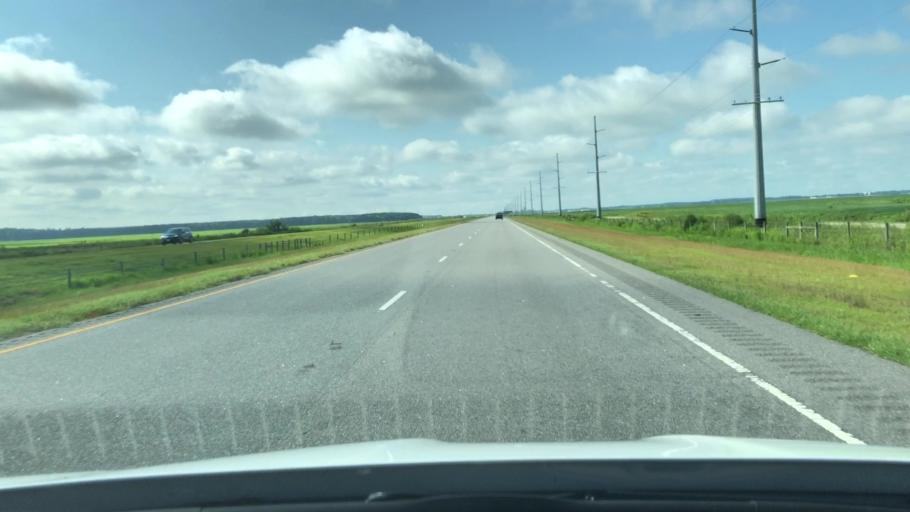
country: US
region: North Carolina
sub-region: Pasquotank County
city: Elizabeth City
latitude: 36.3223
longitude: -76.3098
